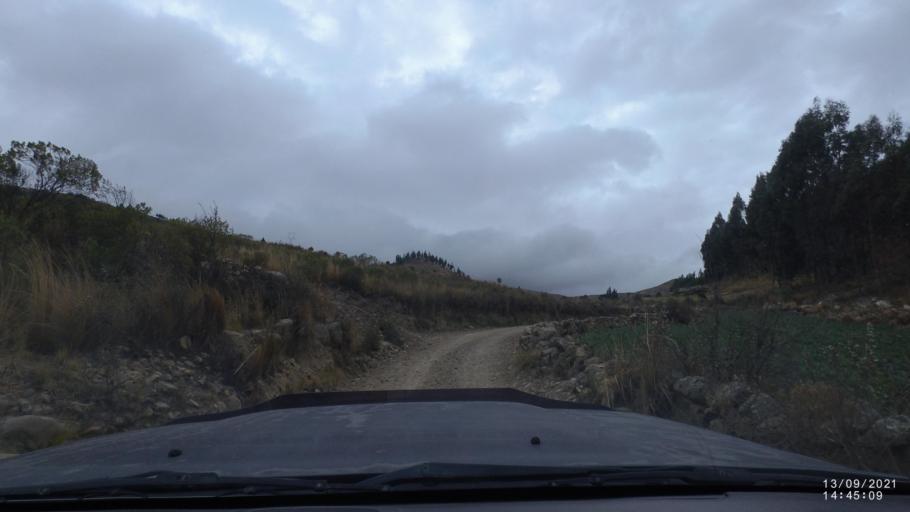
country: BO
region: Cochabamba
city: Colomi
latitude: -17.3545
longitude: -65.8097
